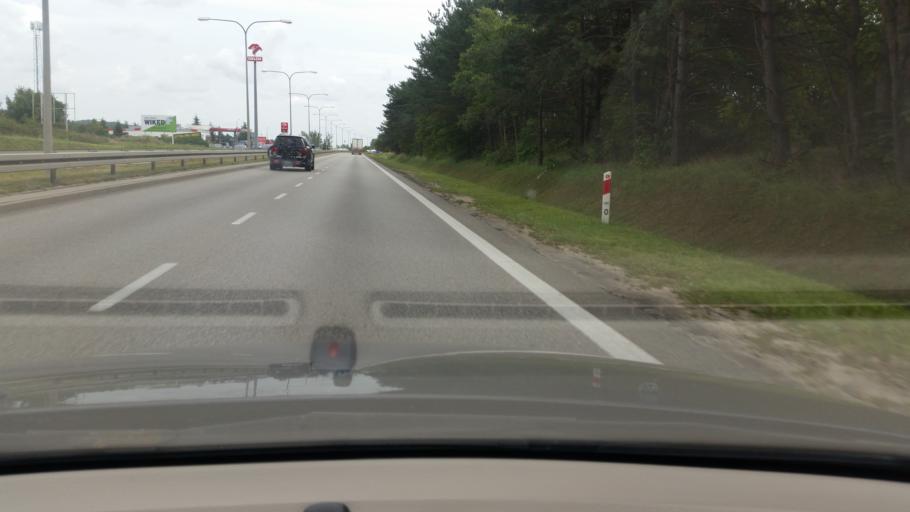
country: PL
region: Pomeranian Voivodeship
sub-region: Powiat wejherowski
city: Bolszewo
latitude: 54.6103
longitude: 18.1865
